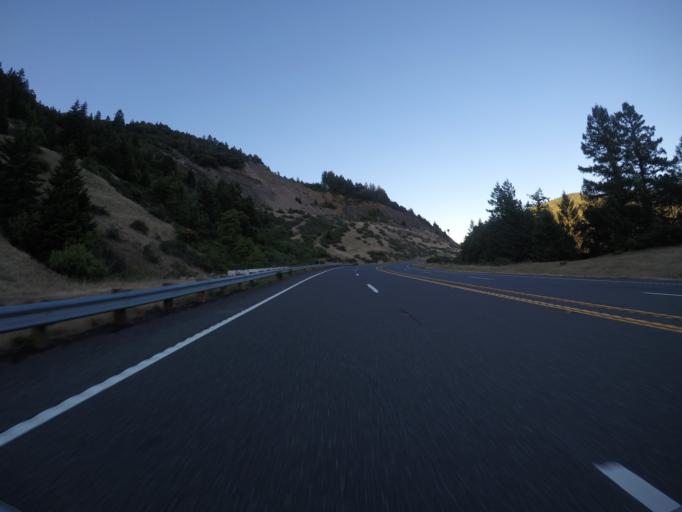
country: US
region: California
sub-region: Mendocino County
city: Laytonville
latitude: 39.8290
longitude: -123.6617
